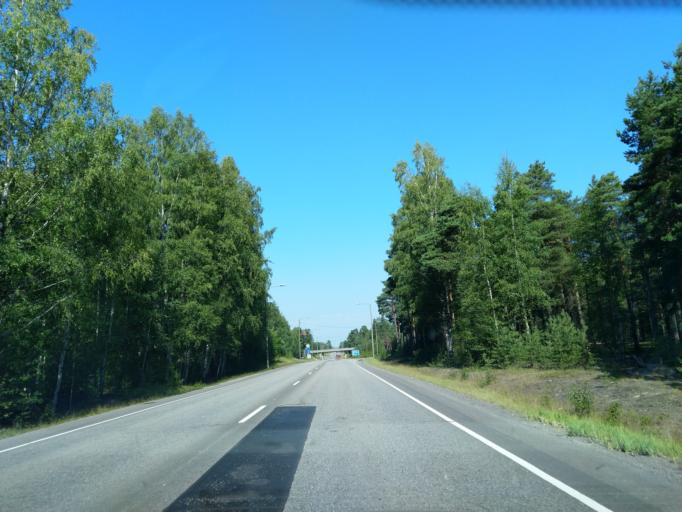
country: FI
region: Satakunta
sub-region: Pori
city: Harjavalta
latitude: 61.3039
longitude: 22.1353
